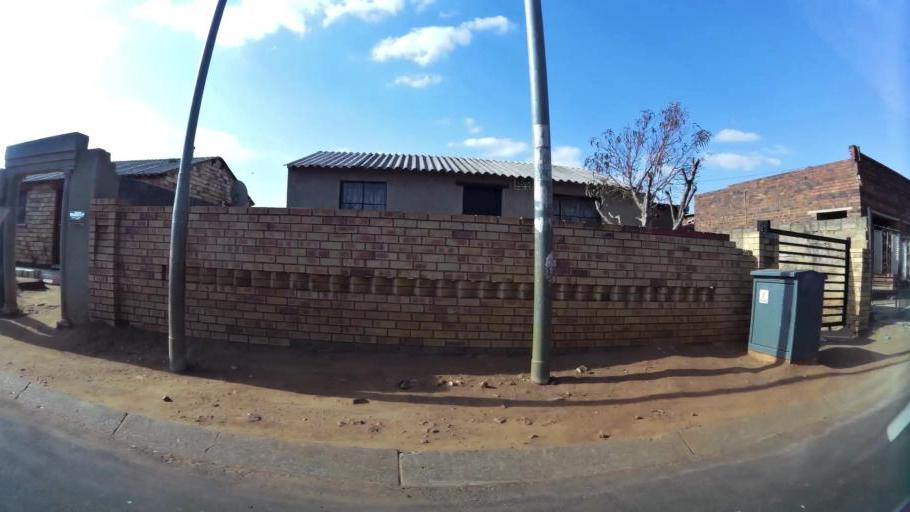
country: ZA
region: Gauteng
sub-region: City of Johannesburg Metropolitan Municipality
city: Soweto
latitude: -26.2550
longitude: 27.9106
